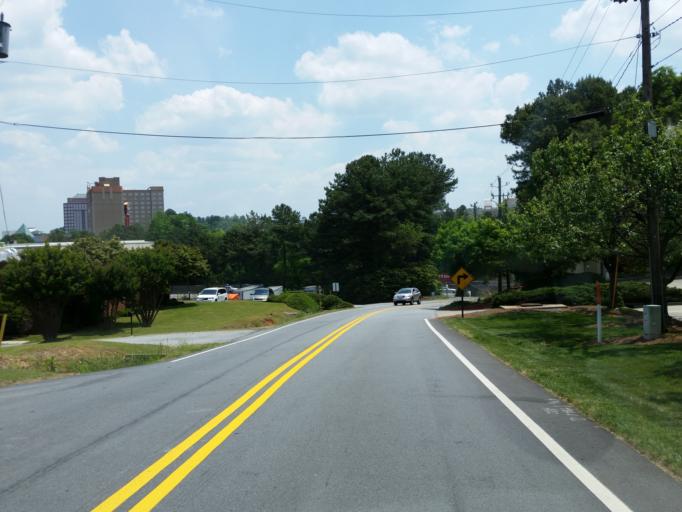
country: US
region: Georgia
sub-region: Cobb County
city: Vinings
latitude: 33.8828
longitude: -84.4739
